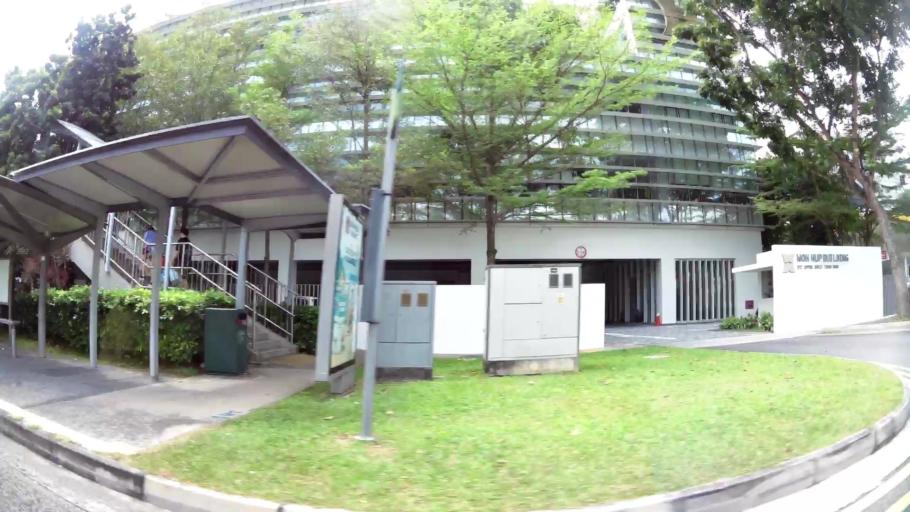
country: SG
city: Singapore
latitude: 1.3459
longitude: 103.7725
